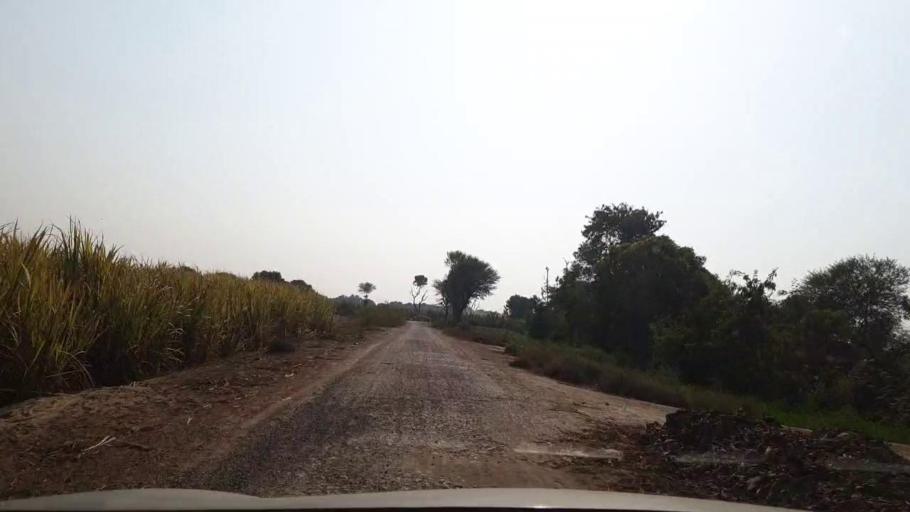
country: PK
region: Sindh
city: Tando Allahyar
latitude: 25.5496
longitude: 68.7744
